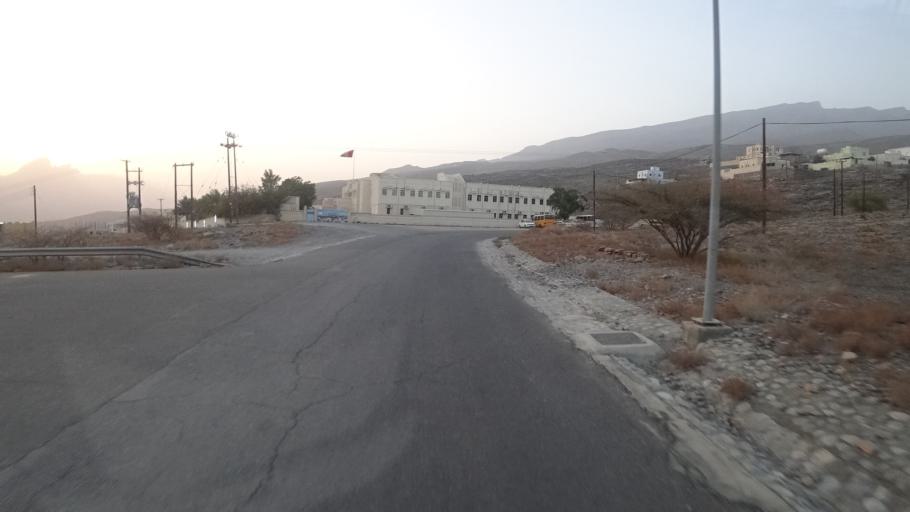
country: OM
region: Muhafazat ad Dakhiliyah
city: Bahla'
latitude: 23.1352
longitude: 57.3038
